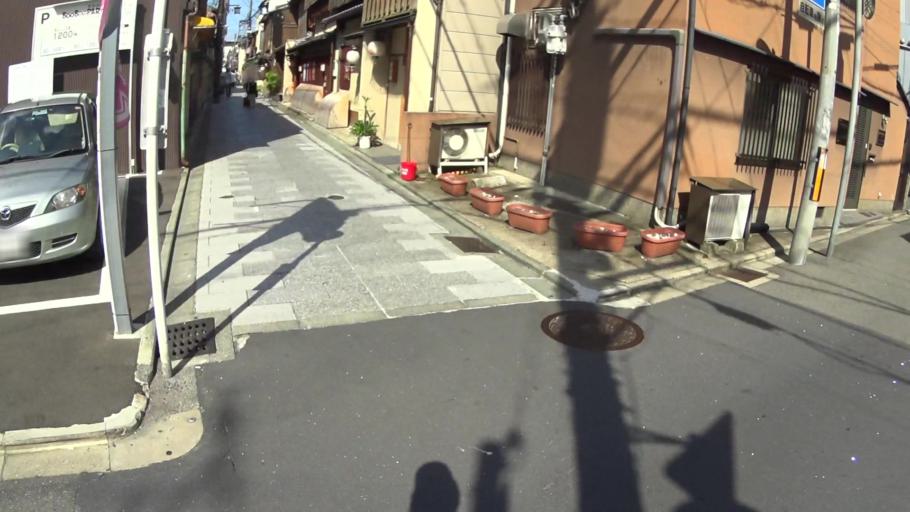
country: JP
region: Kyoto
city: Kyoto
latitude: 34.9991
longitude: 135.7707
